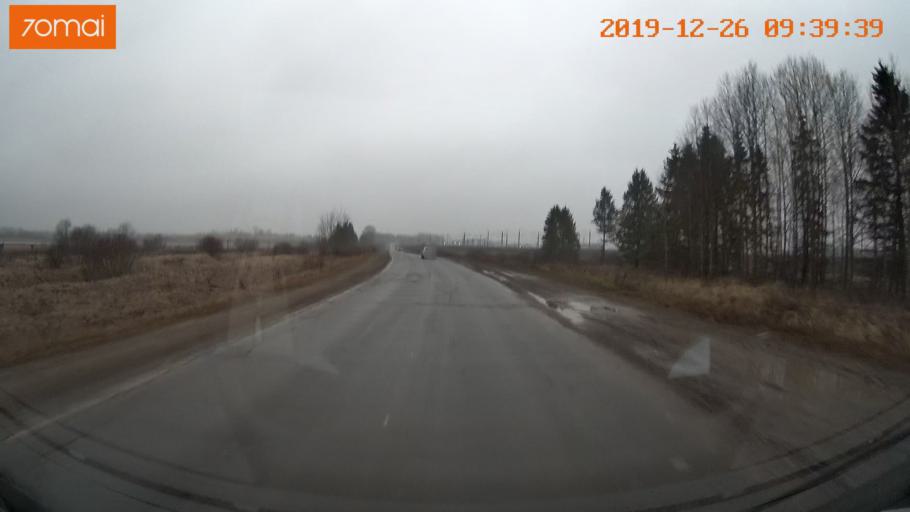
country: RU
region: Vologda
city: Vologda
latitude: 59.1563
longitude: 40.0226
